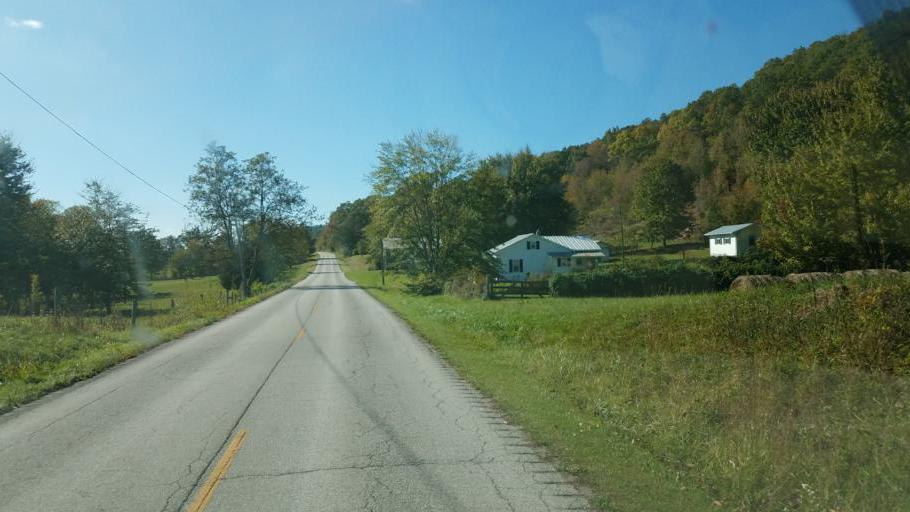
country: US
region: Kentucky
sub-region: Fleming County
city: Flemingsburg
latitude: 38.4686
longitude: -83.5499
